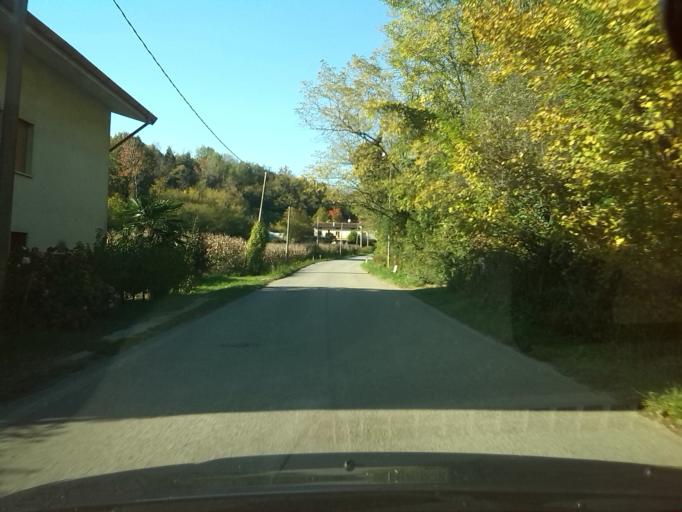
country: IT
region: Friuli Venezia Giulia
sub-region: Provincia di Udine
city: Cividale del Friuli
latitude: 46.0751
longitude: 13.4571
